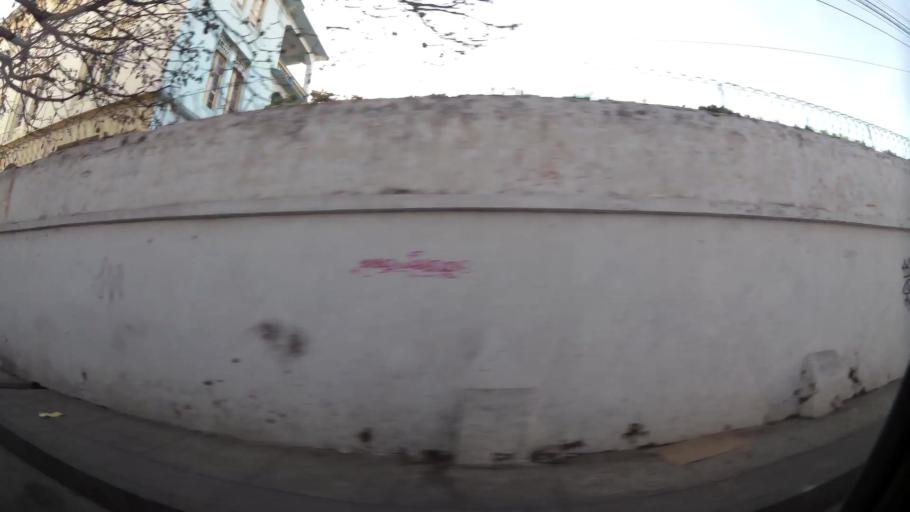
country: CO
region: Atlantico
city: Barranquilla
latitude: 10.9865
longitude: -74.7884
